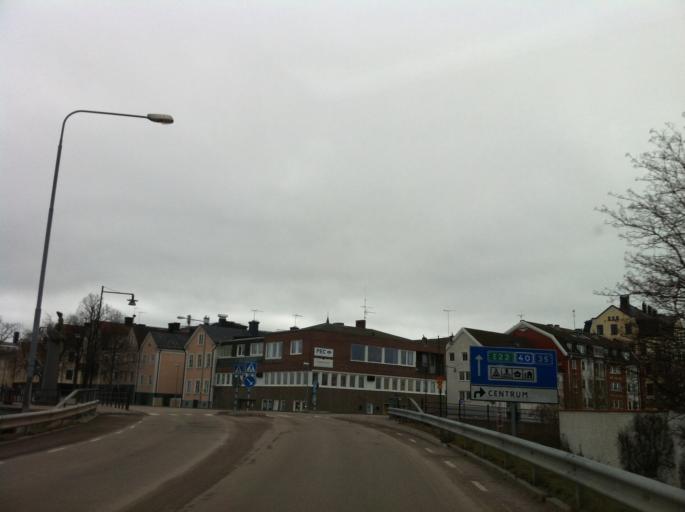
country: SE
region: Kalmar
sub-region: Vasterviks Kommun
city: Vaestervik
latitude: 57.7993
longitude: 16.6124
